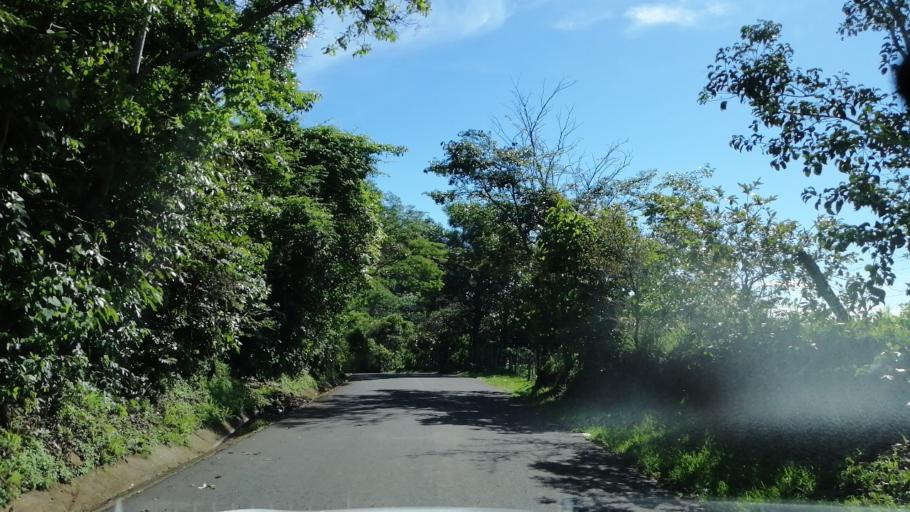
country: SV
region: Morazan
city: Corinto
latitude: 13.8106
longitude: -87.9926
